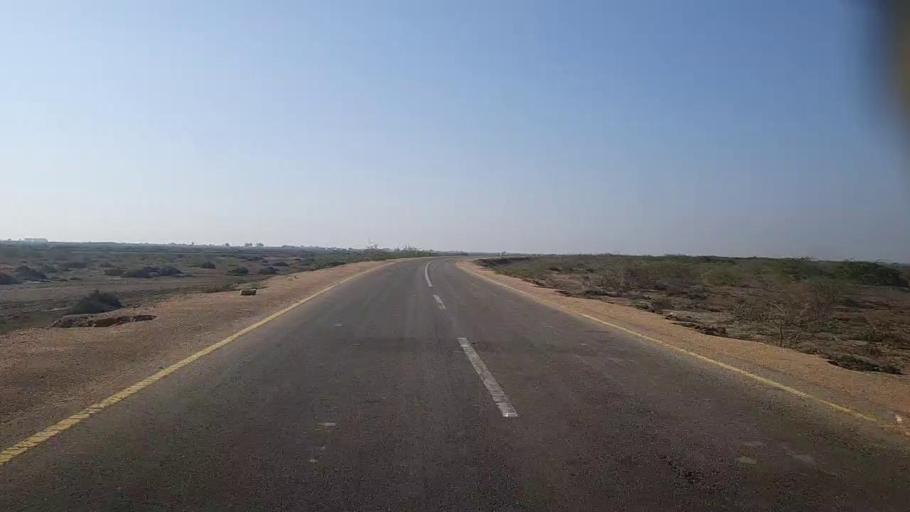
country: PK
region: Sindh
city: Mirpur Sakro
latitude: 24.5619
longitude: 67.4994
